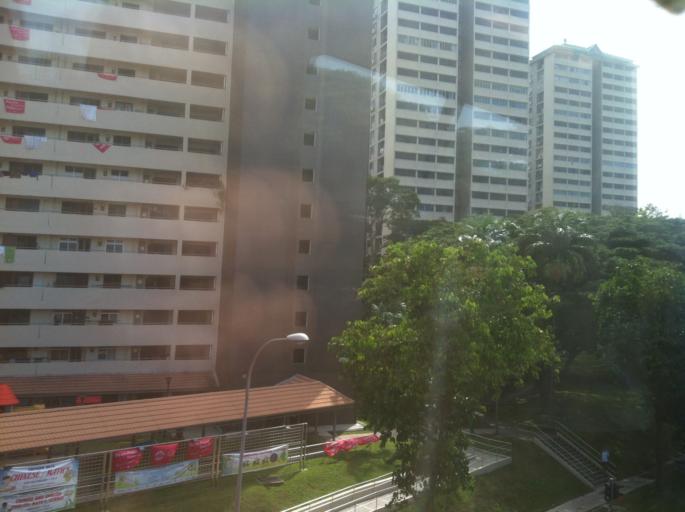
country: SG
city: Singapore
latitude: 1.3233
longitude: 103.9252
